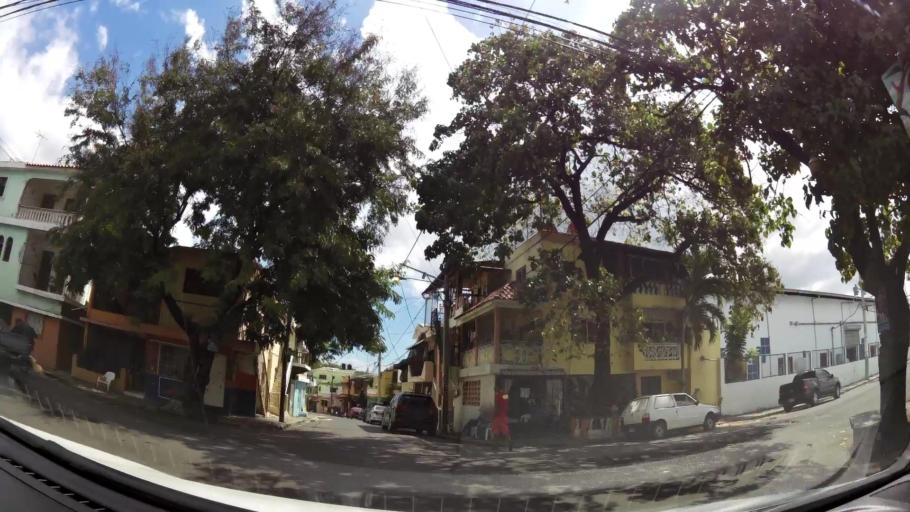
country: DO
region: San Cristobal
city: San Cristobal
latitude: 18.4134
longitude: -70.1150
